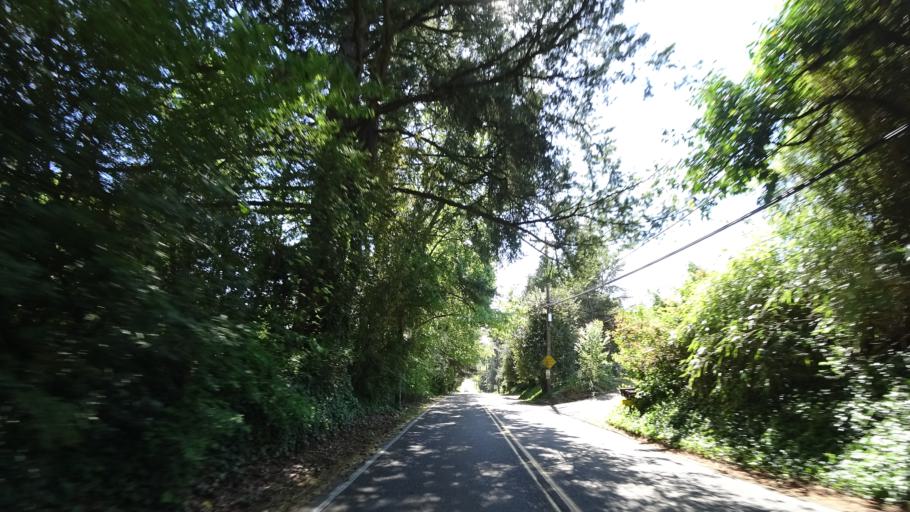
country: US
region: Oregon
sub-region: Washington County
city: Raleigh Hills
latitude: 45.4845
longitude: -122.7346
